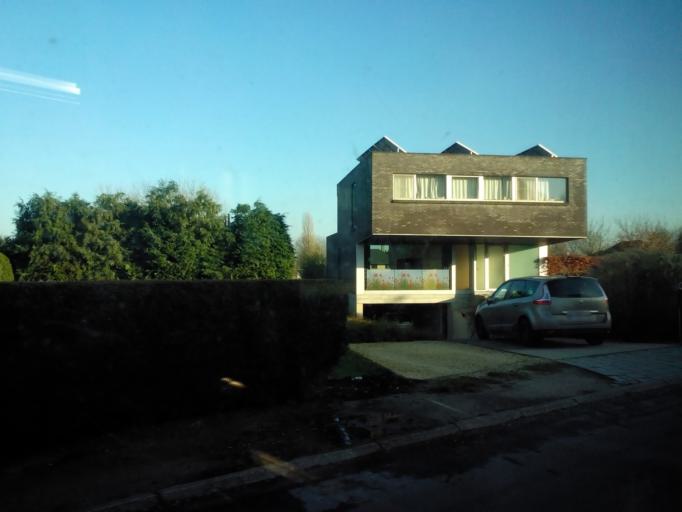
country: BE
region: Flanders
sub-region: Provincie Vlaams-Brabant
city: Bierbeek
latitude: 50.8356
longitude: 4.7293
